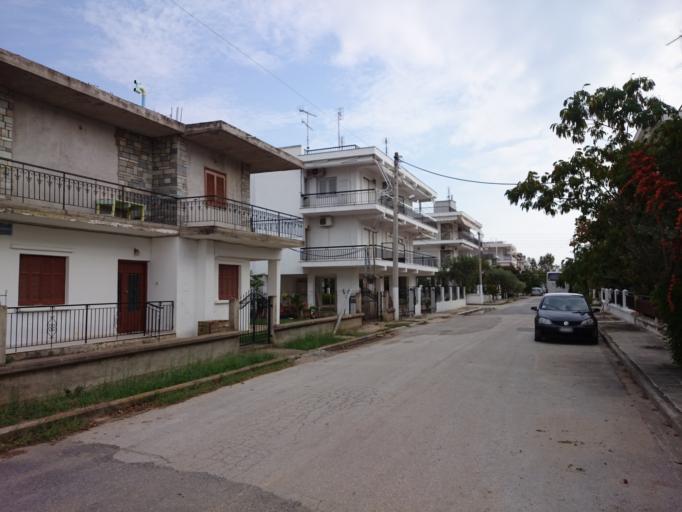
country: GR
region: Central Macedonia
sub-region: Nomos Chalkidikis
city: Nea Flogita
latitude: 40.2520
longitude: 23.2478
